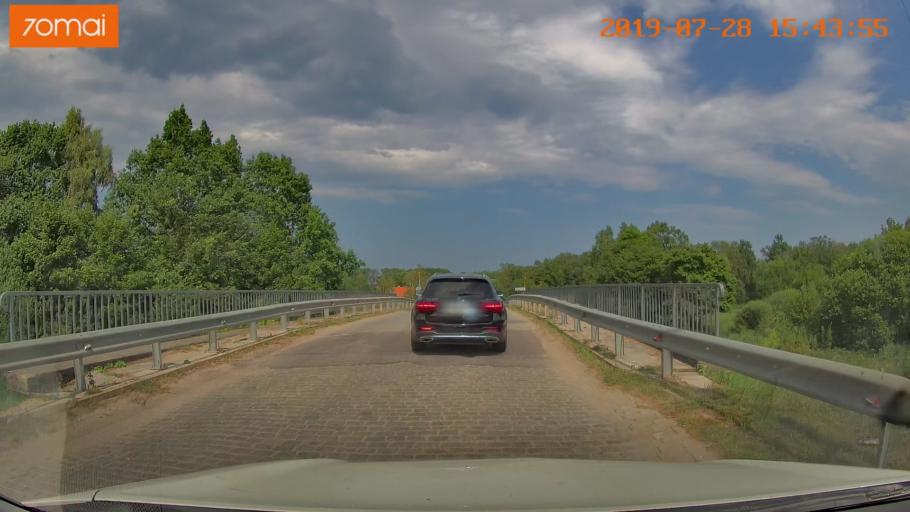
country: RU
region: Kaliningrad
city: Donskoye
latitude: 54.9387
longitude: 20.0278
